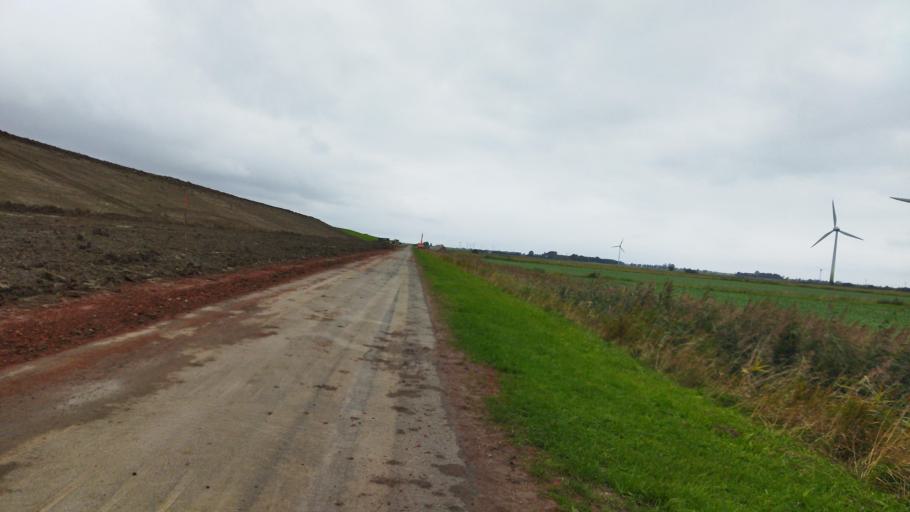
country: NL
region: Groningen
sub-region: Gemeente Delfzijl
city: Delfzijl
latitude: 53.4424
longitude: 7.0201
